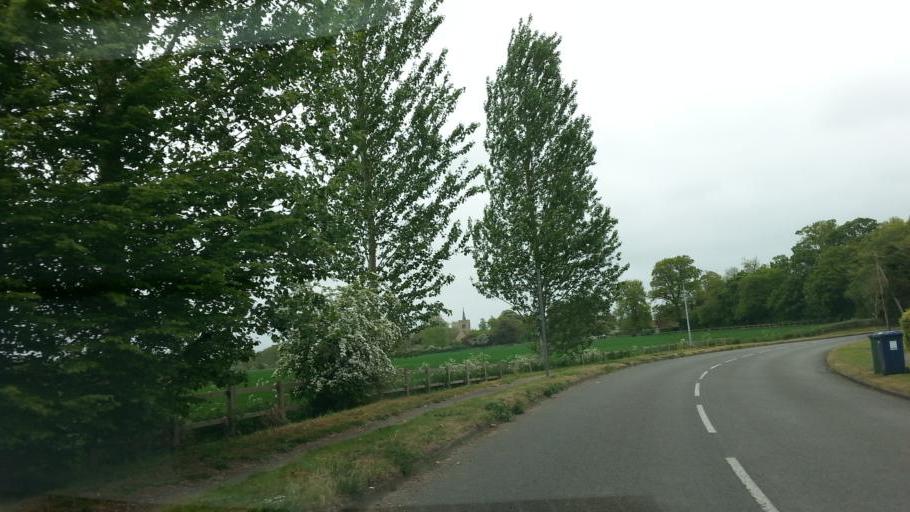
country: GB
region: England
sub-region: Cambridgeshire
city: Sawston
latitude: 52.1155
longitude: 0.1446
